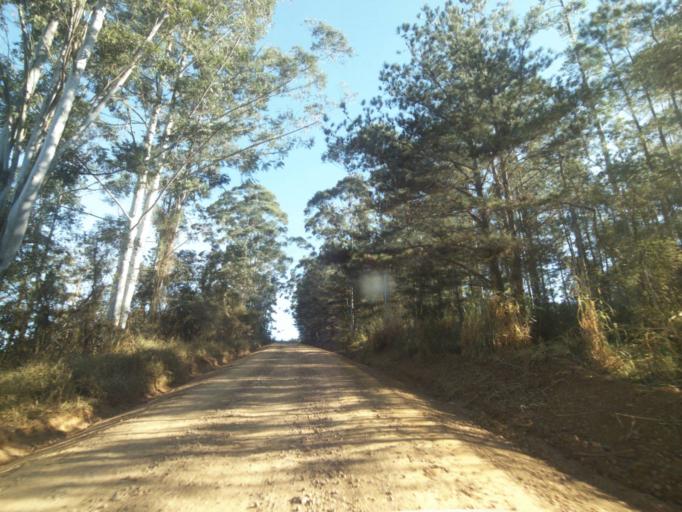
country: BR
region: Parana
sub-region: Tibagi
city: Tibagi
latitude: -24.5250
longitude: -50.5072
